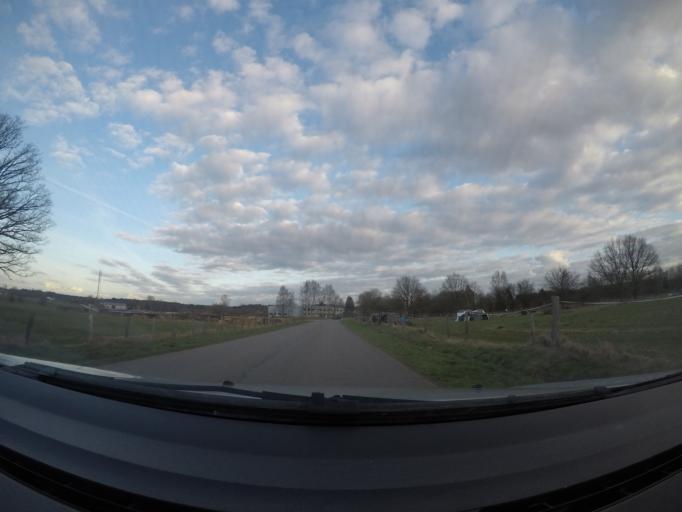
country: BE
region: Wallonia
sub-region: Province du Luxembourg
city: Etalle
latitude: 49.6686
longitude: 5.5688
